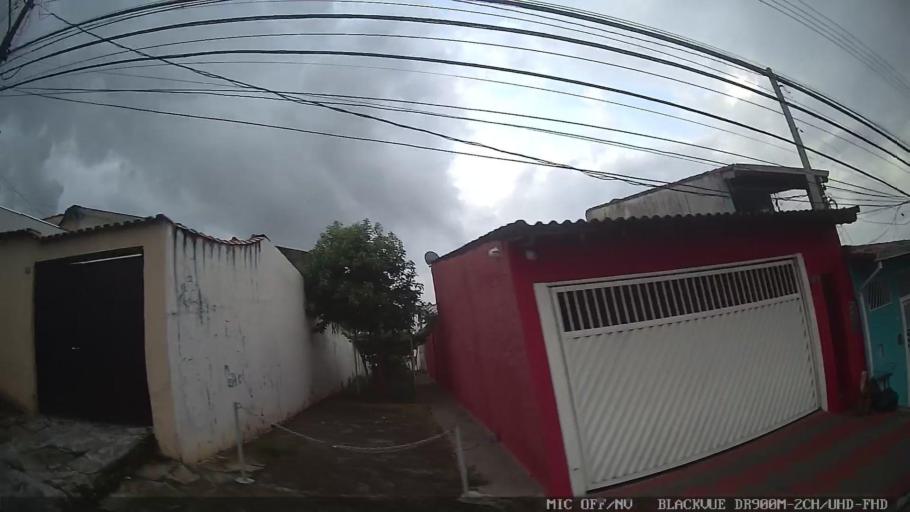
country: BR
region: Sao Paulo
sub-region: Mogi das Cruzes
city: Mogi das Cruzes
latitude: -23.5487
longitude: -46.1967
